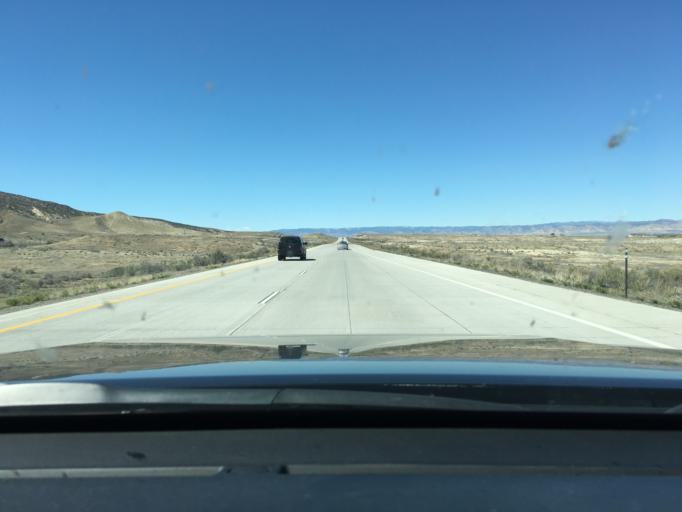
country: US
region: Colorado
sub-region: Mesa County
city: Loma
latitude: 39.1848
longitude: -108.8307
